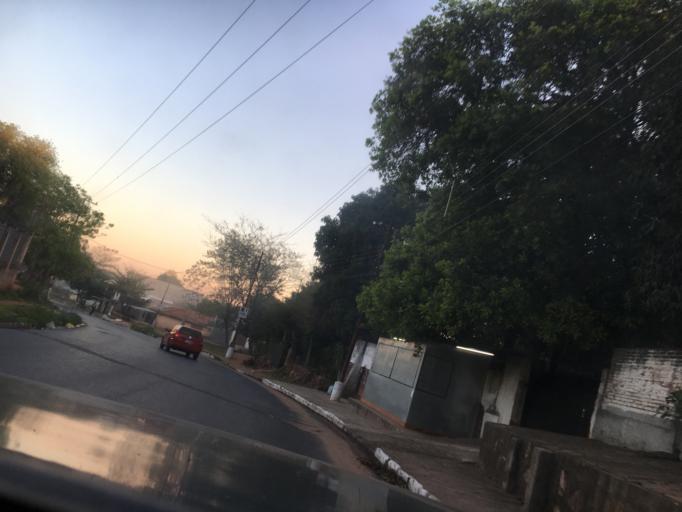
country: PY
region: Central
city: Lambare
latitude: -25.3549
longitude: -57.5996
